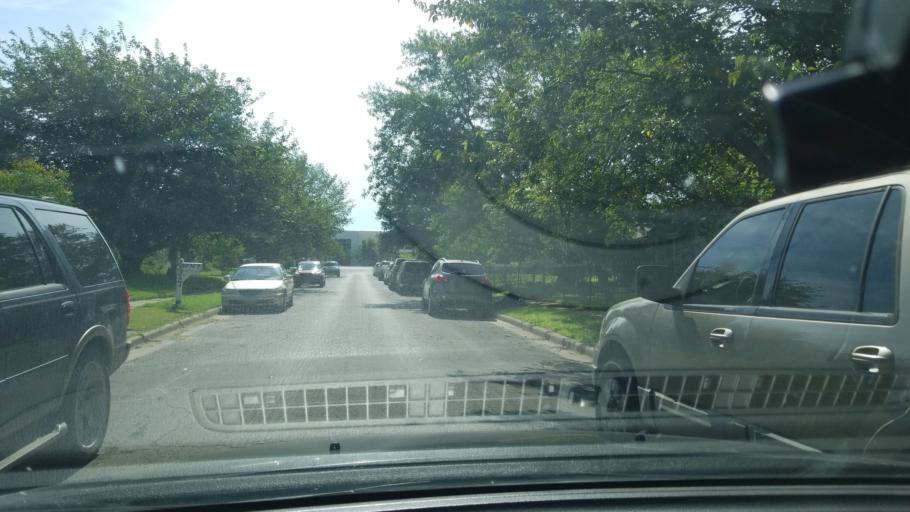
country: US
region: Texas
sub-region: Dallas County
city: Balch Springs
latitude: 32.7257
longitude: -96.6406
